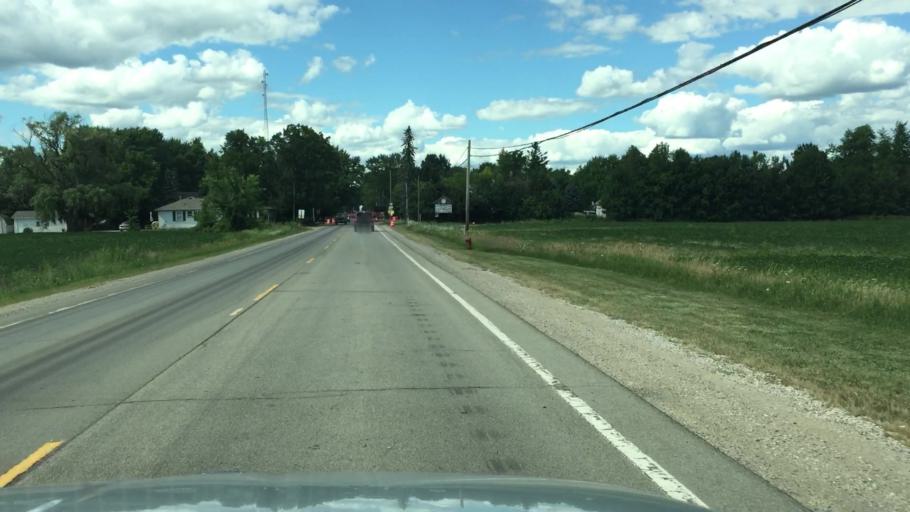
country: US
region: Michigan
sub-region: Saint Clair County
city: Capac
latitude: 43.0037
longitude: -82.9282
